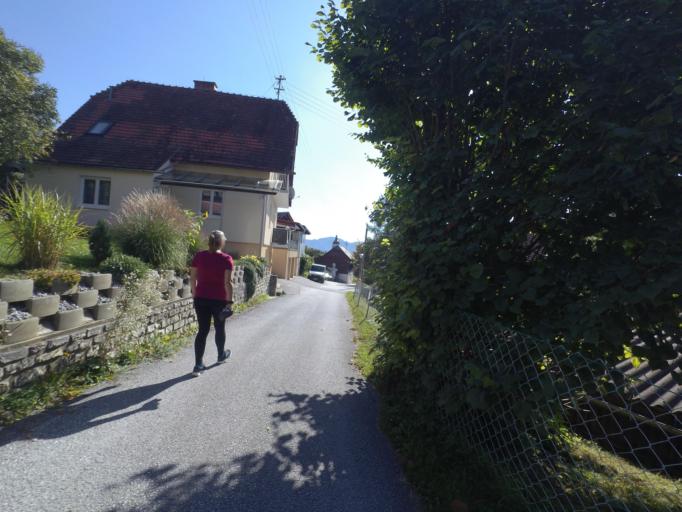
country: AT
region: Styria
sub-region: Politischer Bezirk Weiz
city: Passail
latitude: 47.2874
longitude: 15.4746
